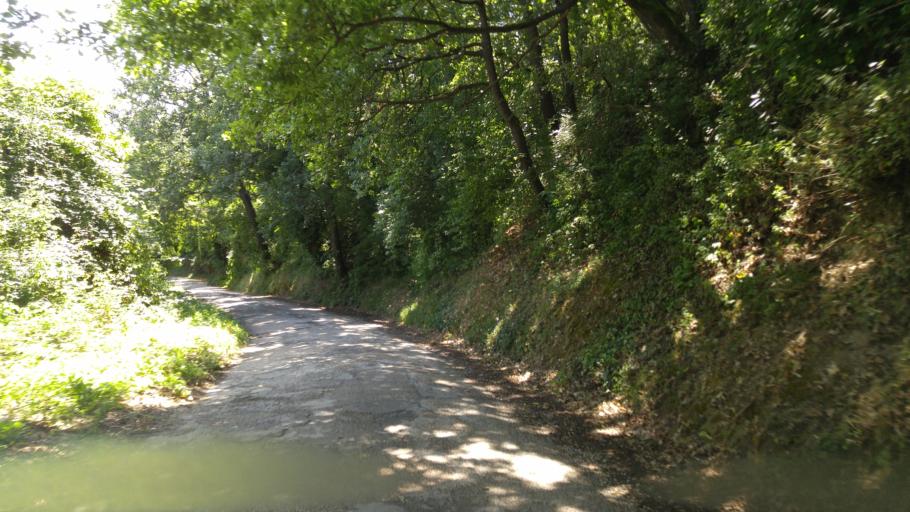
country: IT
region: The Marches
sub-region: Provincia di Pesaro e Urbino
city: Fenile
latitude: 43.8223
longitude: 12.9722
